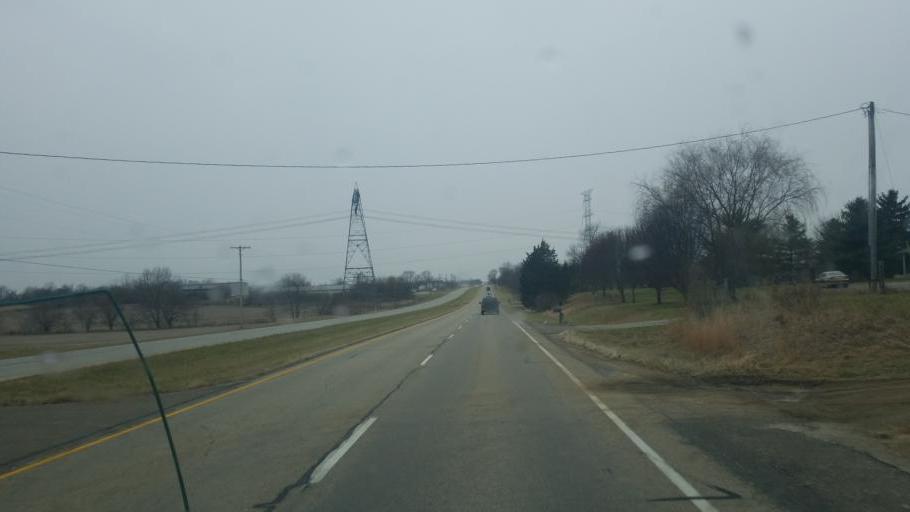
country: US
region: Indiana
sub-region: Hancock County
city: Greenfield
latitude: 39.7899
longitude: -85.6621
